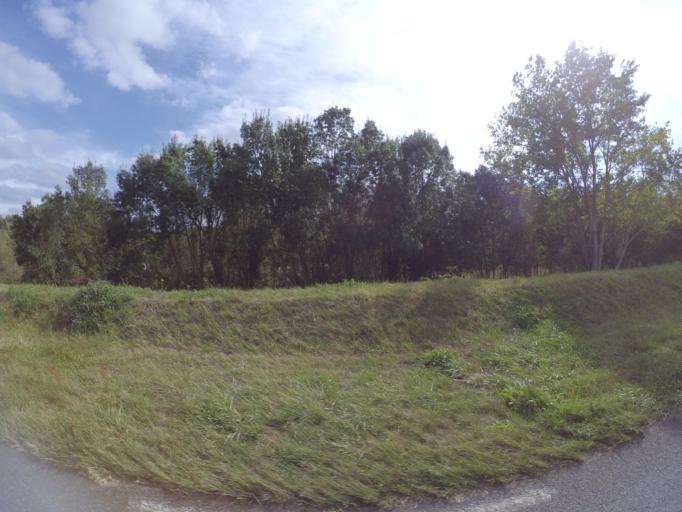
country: FR
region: Centre
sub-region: Departement d'Indre-et-Loire
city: Huismes
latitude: 47.2725
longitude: 0.3041
